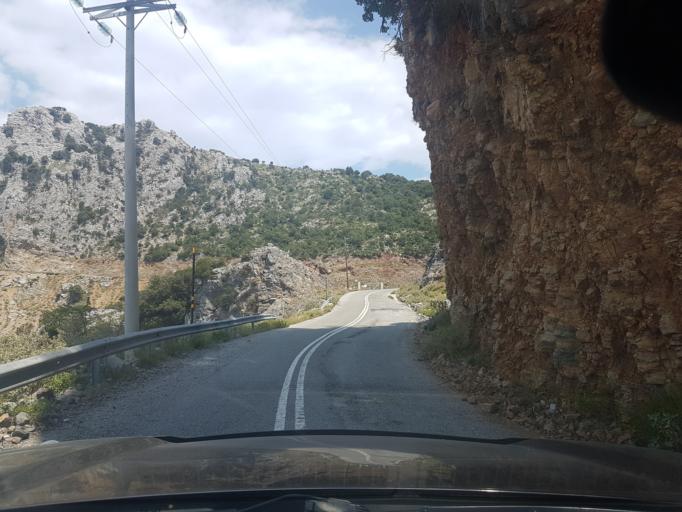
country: GR
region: Central Greece
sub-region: Nomos Evvoias
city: Kymi
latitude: 38.6513
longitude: 23.9662
